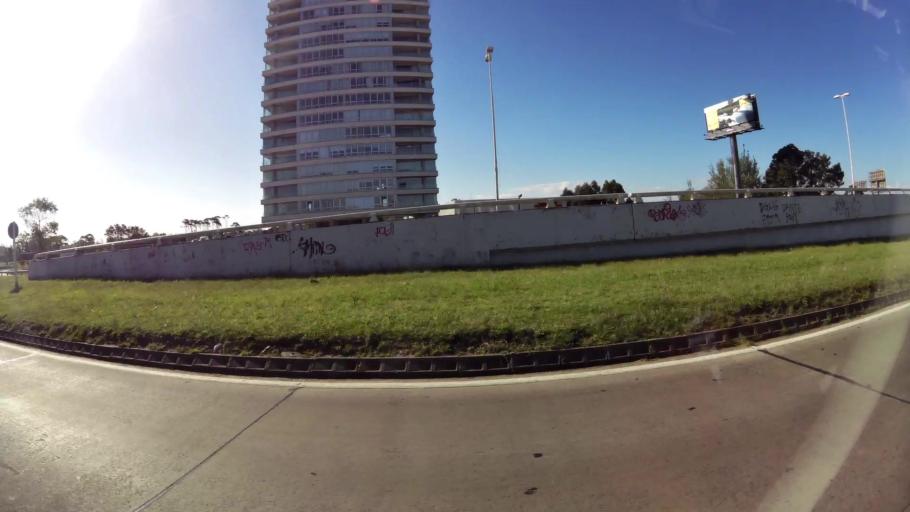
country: UY
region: Canelones
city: Barra de Carrasco
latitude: -34.8750
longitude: -56.0334
